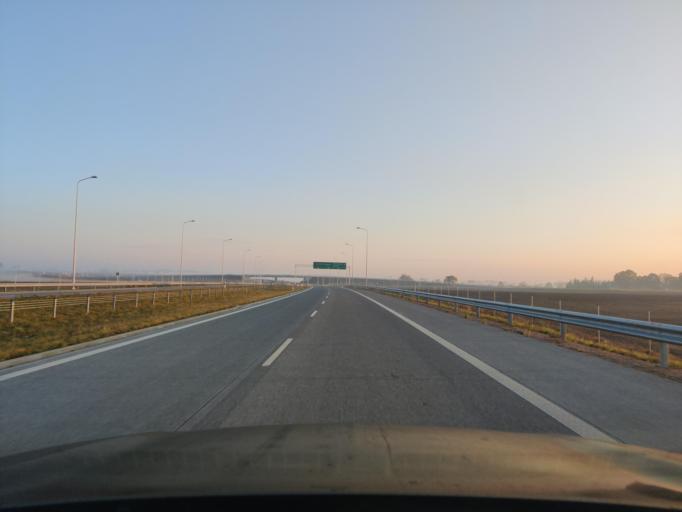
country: PL
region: Masovian Voivodeship
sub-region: Powiat mlawski
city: Wisniewo
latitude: 52.9853
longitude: 20.3431
